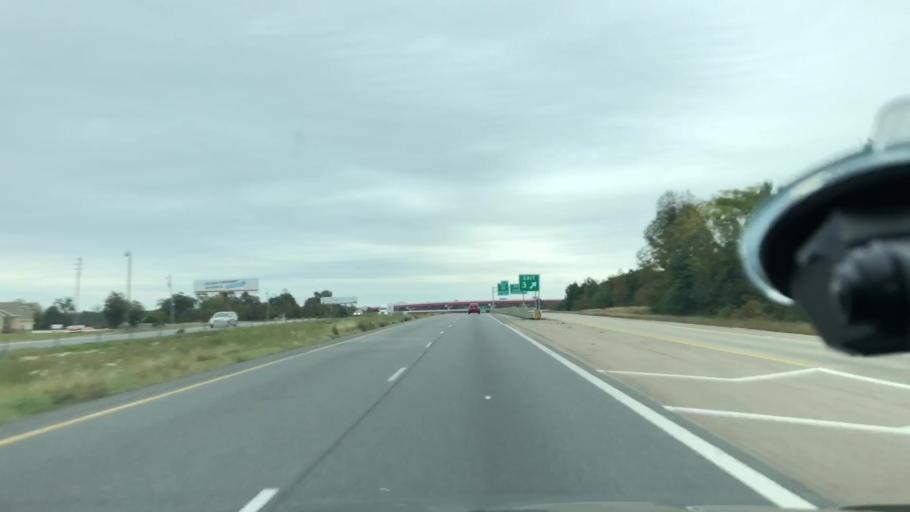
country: US
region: Arkansas
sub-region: Miller County
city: Texarkana
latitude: 33.4780
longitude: -93.9953
